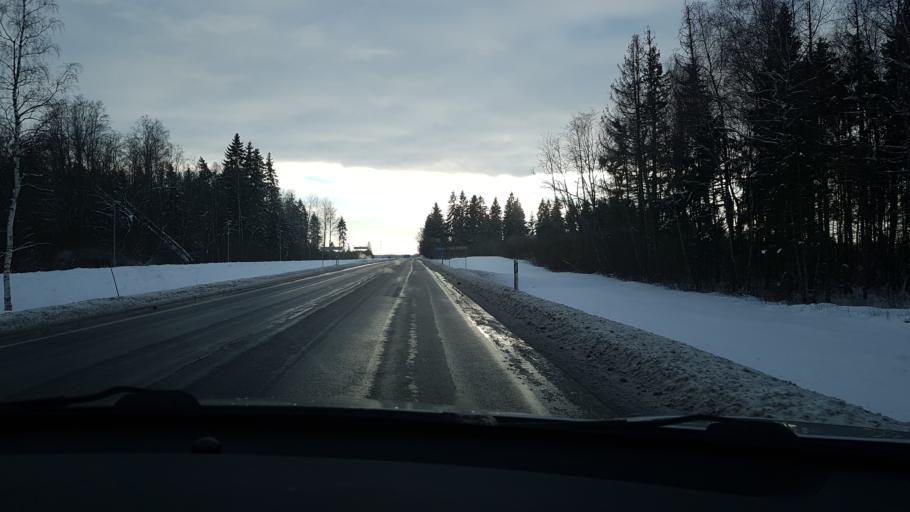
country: EE
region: Jaervamaa
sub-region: Paide linn
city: Paide
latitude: 58.9291
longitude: 25.6297
